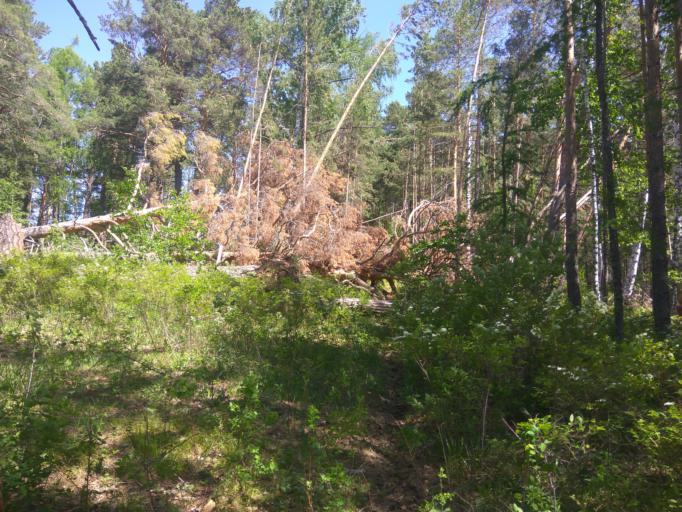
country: RU
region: Krasnoyarskiy
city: Krasnoyarsk
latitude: 55.9121
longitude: 92.9394
